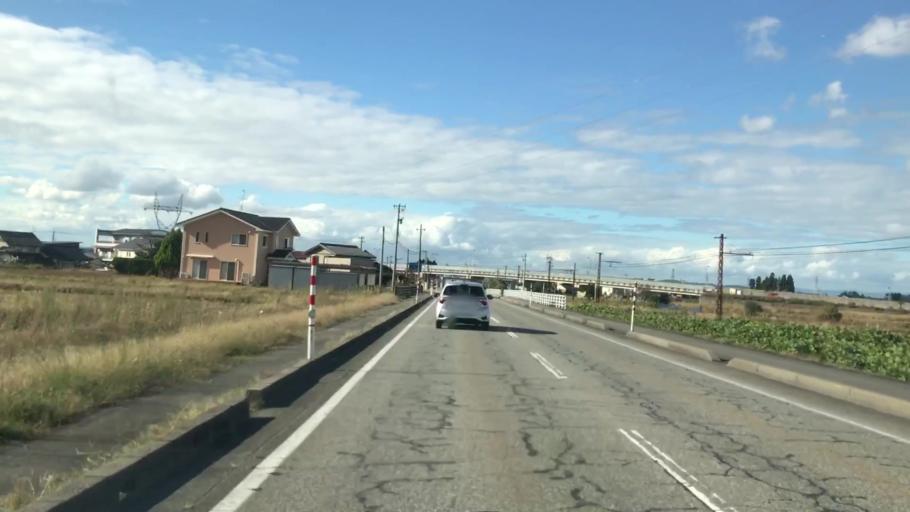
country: JP
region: Toyama
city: Toyama-shi
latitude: 36.6326
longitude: 137.2484
